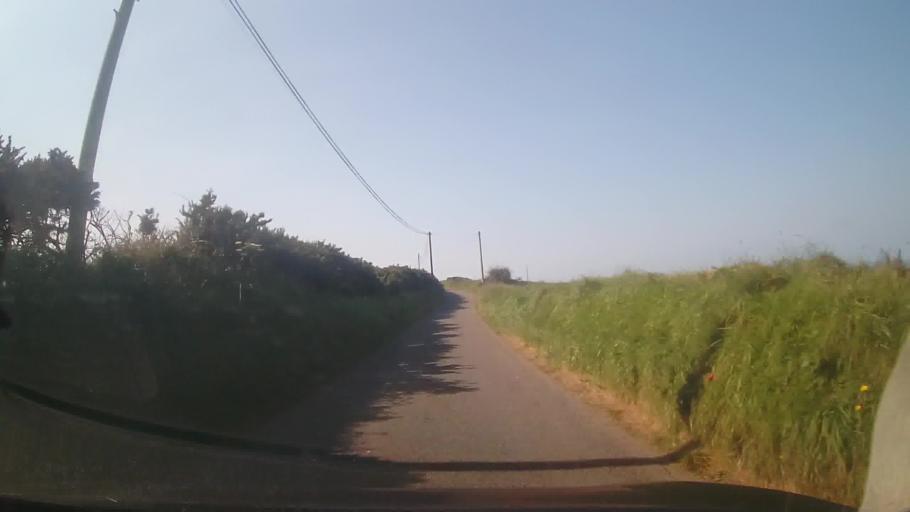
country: GB
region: Wales
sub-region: Pembrokeshire
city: Llanrhian
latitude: 51.9281
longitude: -5.1658
